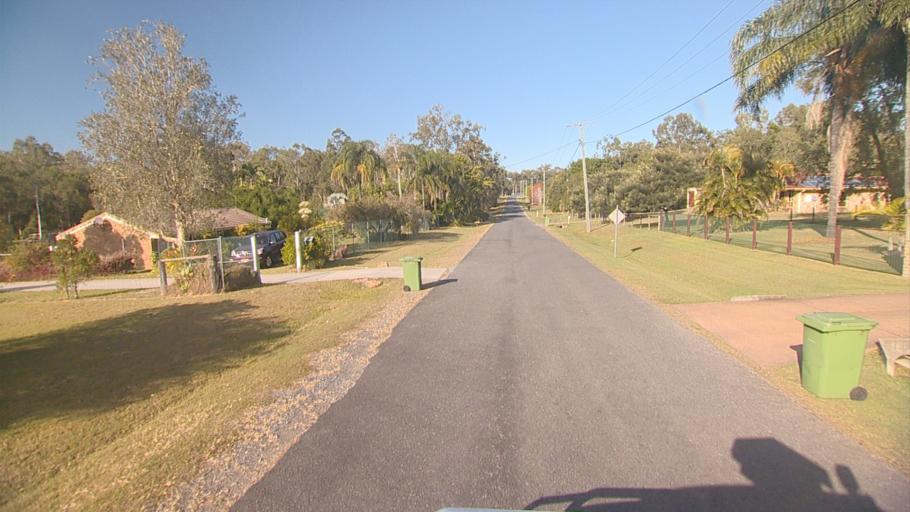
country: AU
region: Queensland
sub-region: Logan
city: Park Ridge South
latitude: -27.7431
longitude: 153.0295
